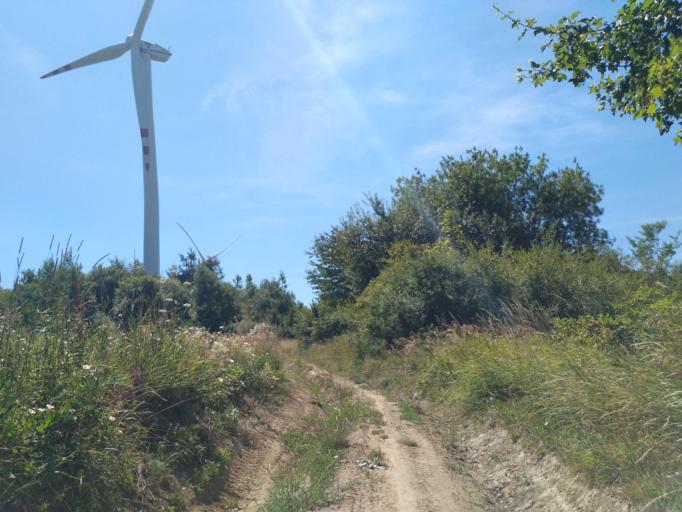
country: PL
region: Subcarpathian Voivodeship
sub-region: Powiat sanocki
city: Bukowsko
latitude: 49.5124
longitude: 22.0549
